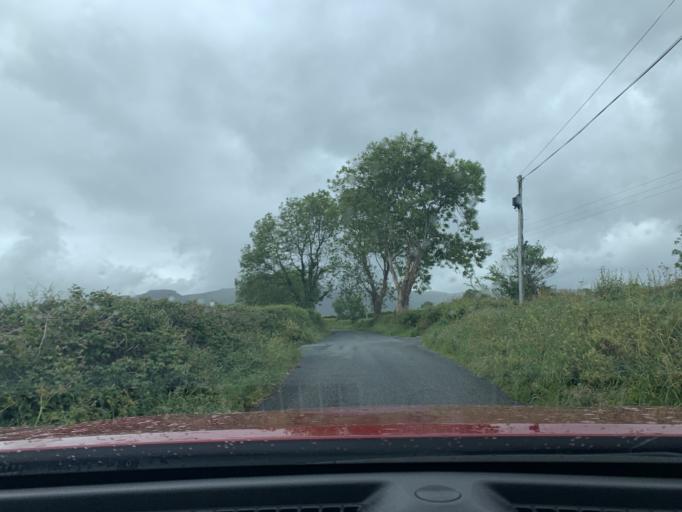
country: IE
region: Connaught
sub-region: Sligo
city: Sligo
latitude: 54.3060
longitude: -8.4558
